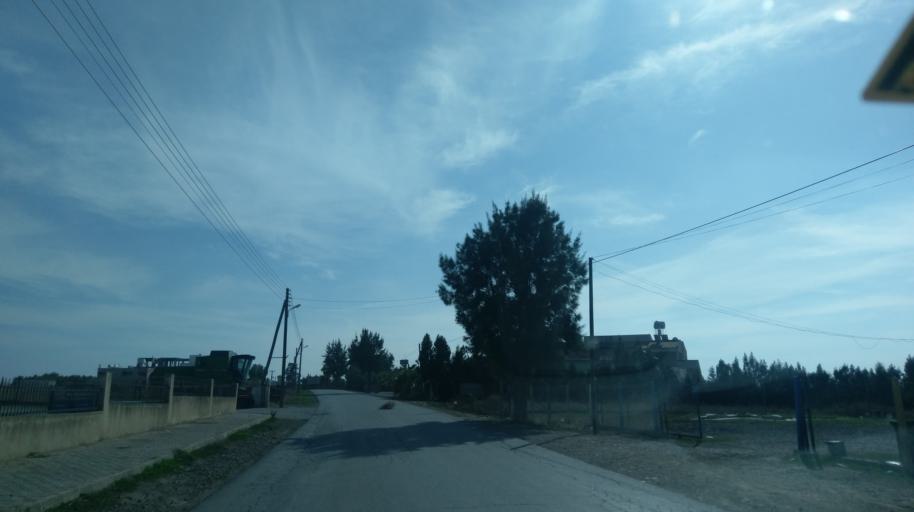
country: CY
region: Larnaka
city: Pergamos
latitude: 35.1277
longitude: 33.6619
